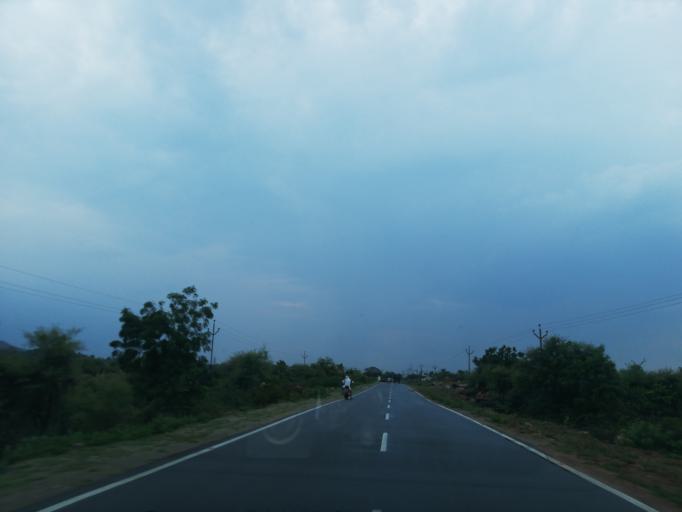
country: IN
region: Andhra Pradesh
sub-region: Guntur
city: Macherla
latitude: 16.6690
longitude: 79.2809
